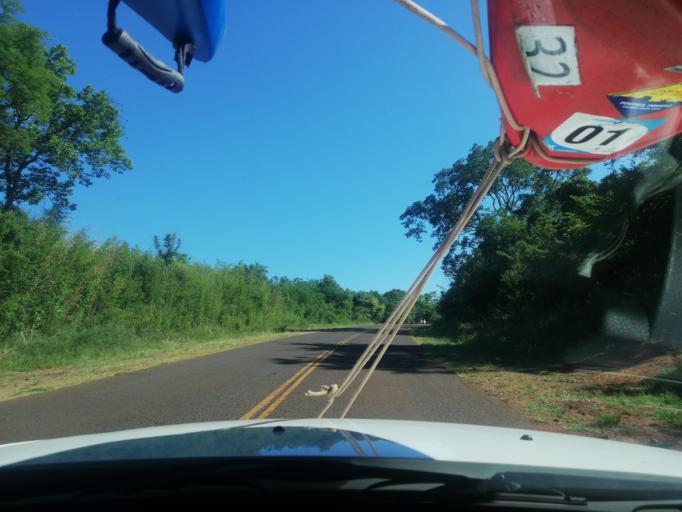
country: AR
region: Misiones
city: Santa Ana
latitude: -27.3584
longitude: -55.5871
